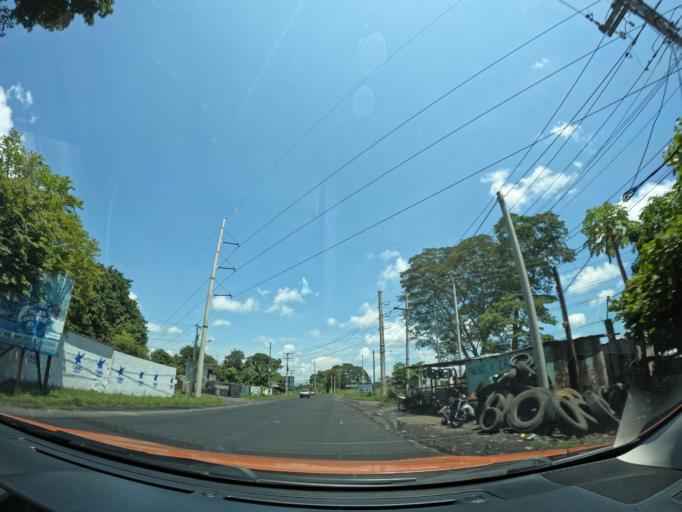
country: GT
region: Escuintla
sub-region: Municipio de Masagua
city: Masagua
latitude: 14.2017
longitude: -90.8452
